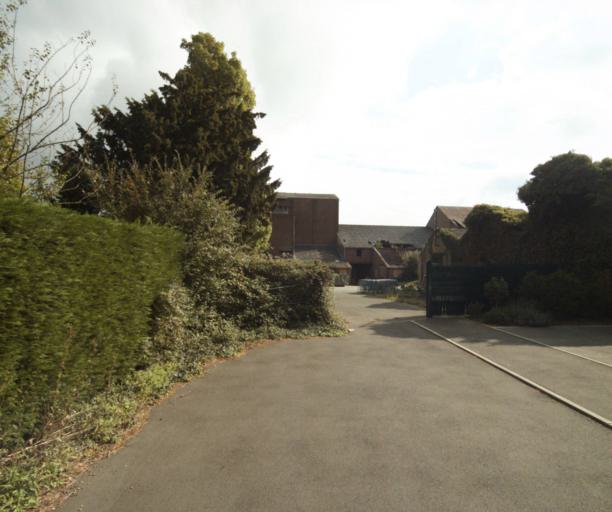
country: FR
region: Nord-Pas-de-Calais
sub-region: Departement du Nord
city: Herlies
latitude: 50.5805
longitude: 2.8510
